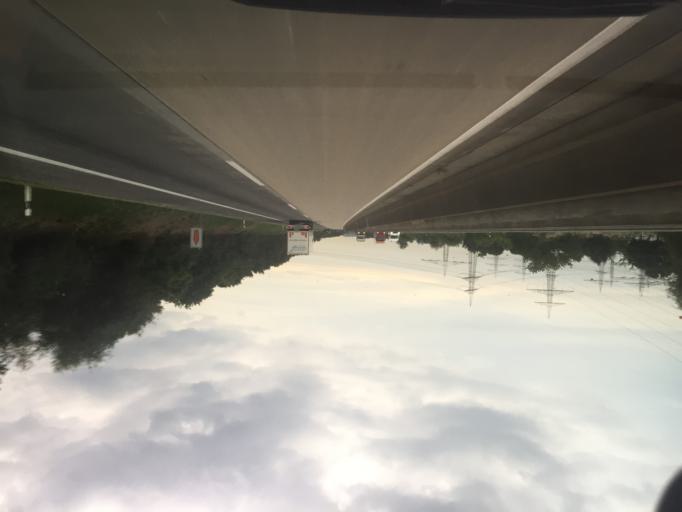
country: DE
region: North Rhine-Westphalia
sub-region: Regierungsbezirk Koln
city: Elsdorf
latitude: 50.9517
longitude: 6.5921
